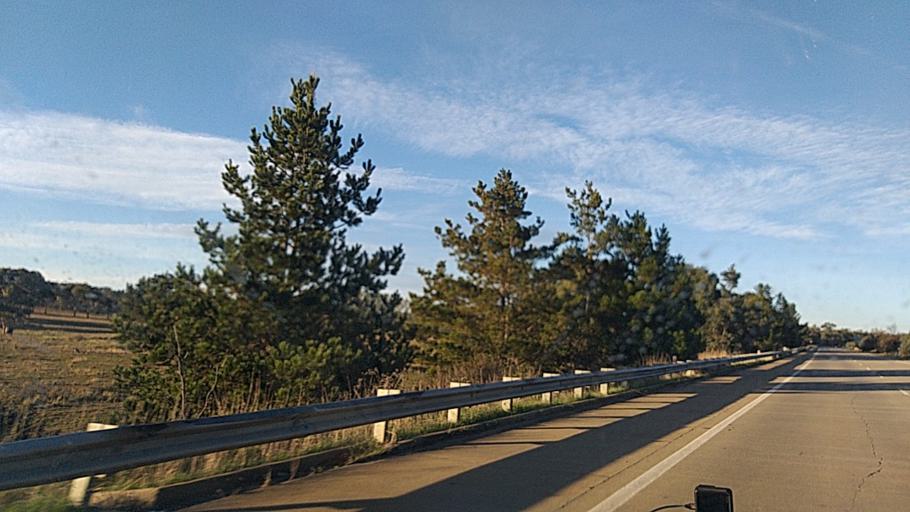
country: AU
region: New South Wales
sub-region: Yass Valley
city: Gundaroo
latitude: -35.1478
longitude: 149.3320
